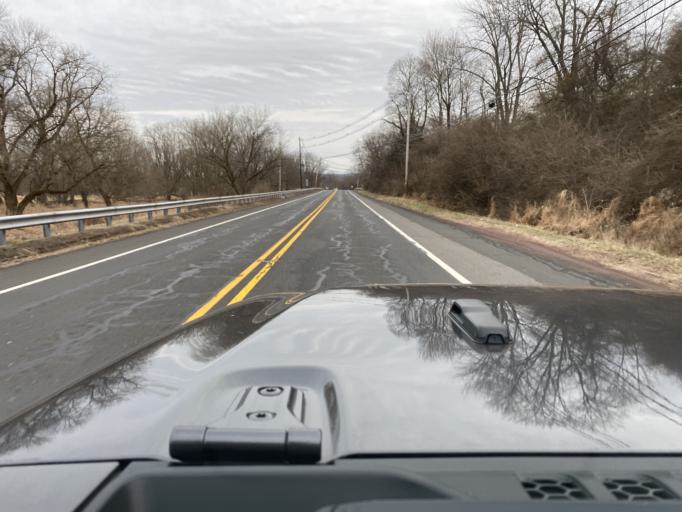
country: US
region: New Jersey
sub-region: Somerset County
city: Bloomingdale
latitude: 40.5193
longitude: -74.7353
